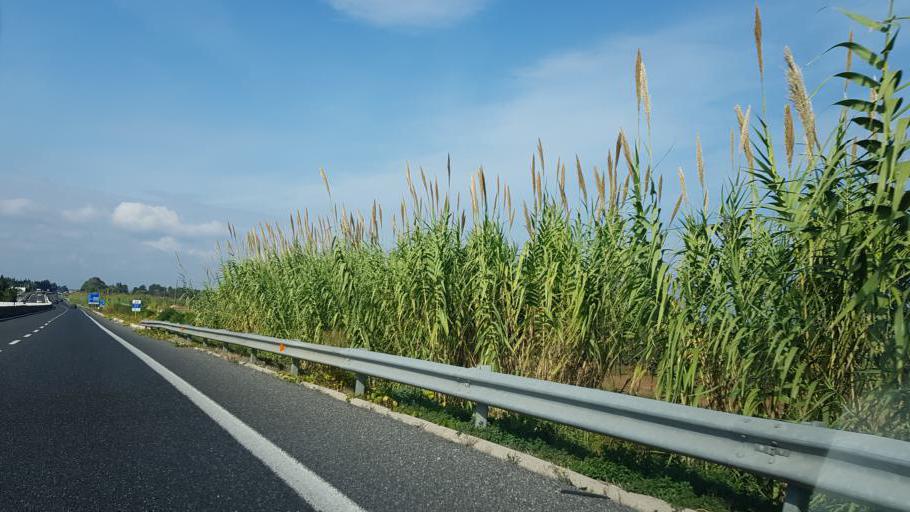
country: IT
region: Apulia
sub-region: Provincia di Brindisi
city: Brindisi
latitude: 40.6674
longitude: 17.8705
